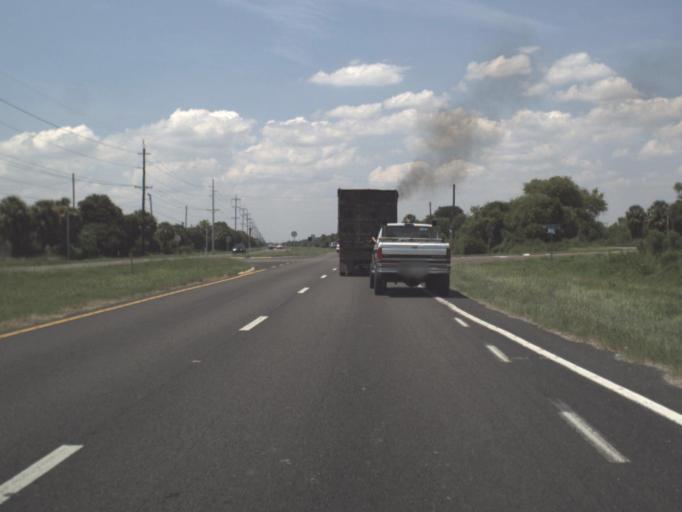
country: US
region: Florida
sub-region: Hillsborough County
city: Gibsonton
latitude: 27.8668
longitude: -82.3861
